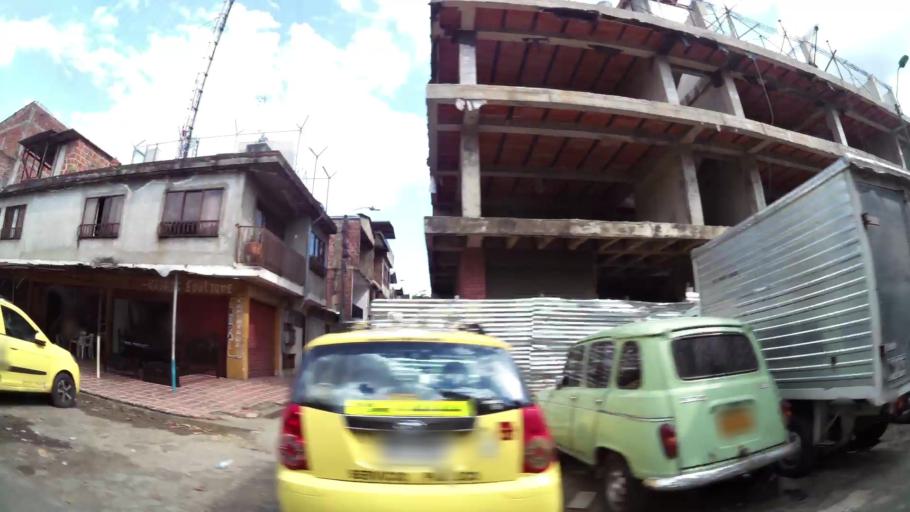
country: CO
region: Valle del Cauca
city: Cali
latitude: 3.3964
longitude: -76.5130
